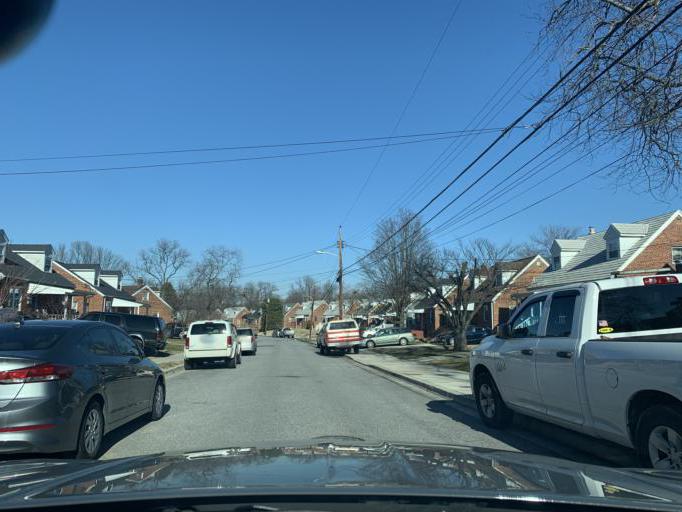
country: US
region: Maryland
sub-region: Anne Arundel County
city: Glen Burnie
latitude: 39.1629
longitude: -76.6182
